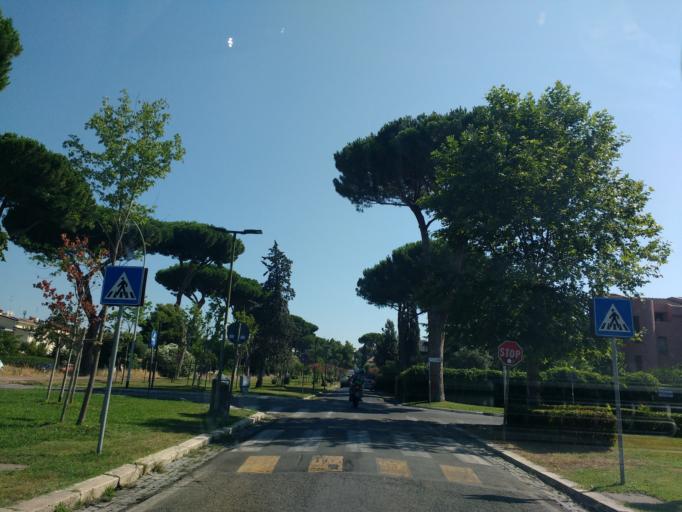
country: IT
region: Latium
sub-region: Citta metropolitana di Roma Capitale
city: Acilia-Castel Fusano-Ostia Antica
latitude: 41.7660
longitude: 12.3686
